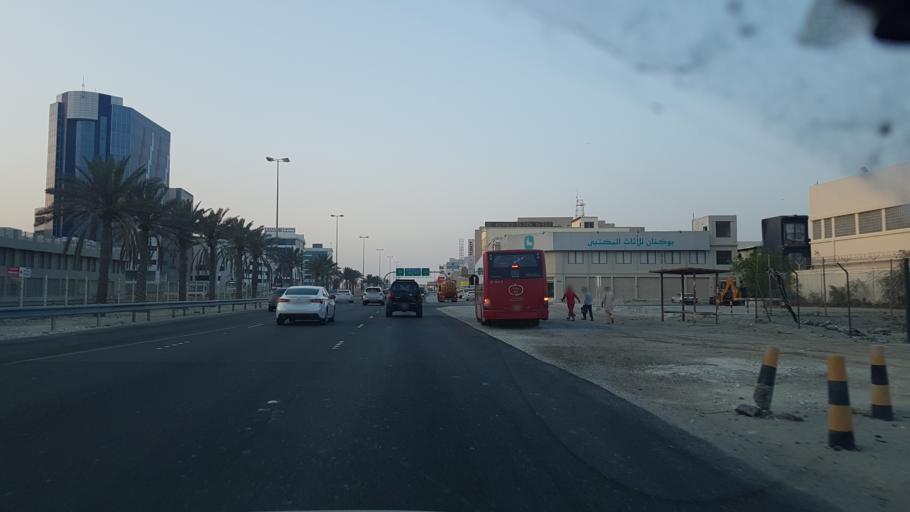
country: BH
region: Northern
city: Ar Rifa'
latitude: 26.1333
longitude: 50.5855
